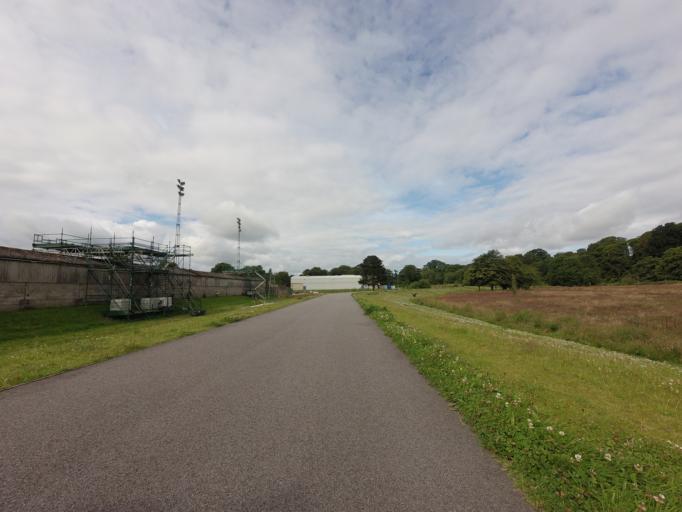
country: GB
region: Scotland
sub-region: Moray
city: Elgin
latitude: 57.6525
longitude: -3.3208
